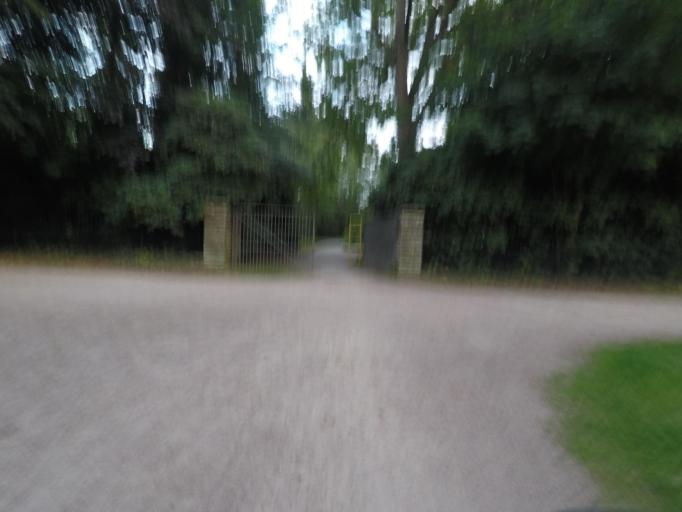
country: DE
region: Hamburg
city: Wellingsbuettel
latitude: 53.6302
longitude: 10.0688
